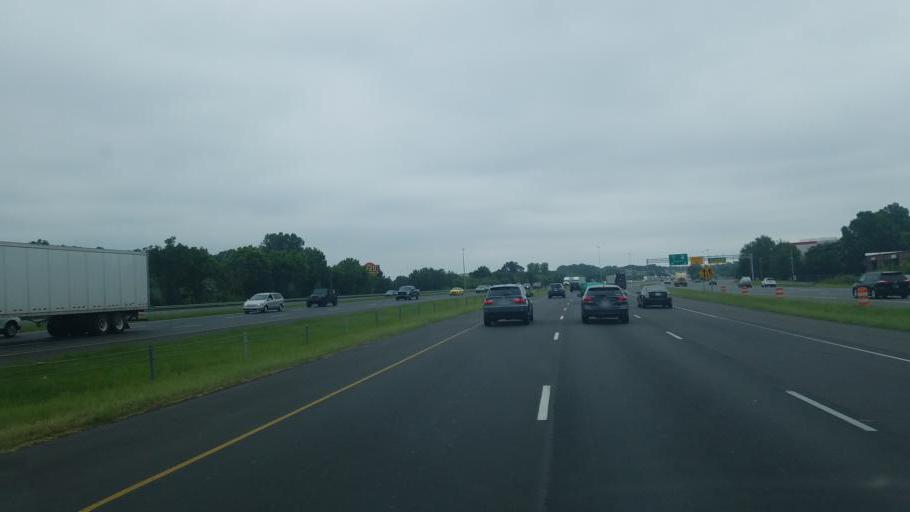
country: US
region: North Carolina
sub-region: Mecklenburg County
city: Pineville
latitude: 35.1325
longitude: -80.9125
